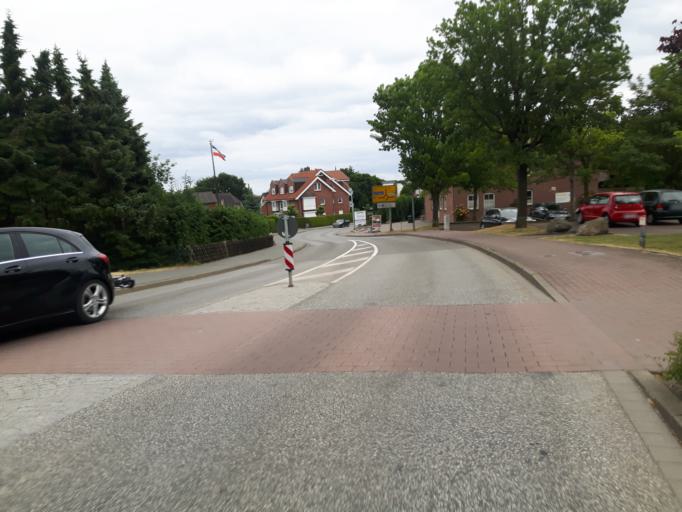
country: DE
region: Schleswig-Holstein
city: Gromitz
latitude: 54.1504
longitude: 10.9602
